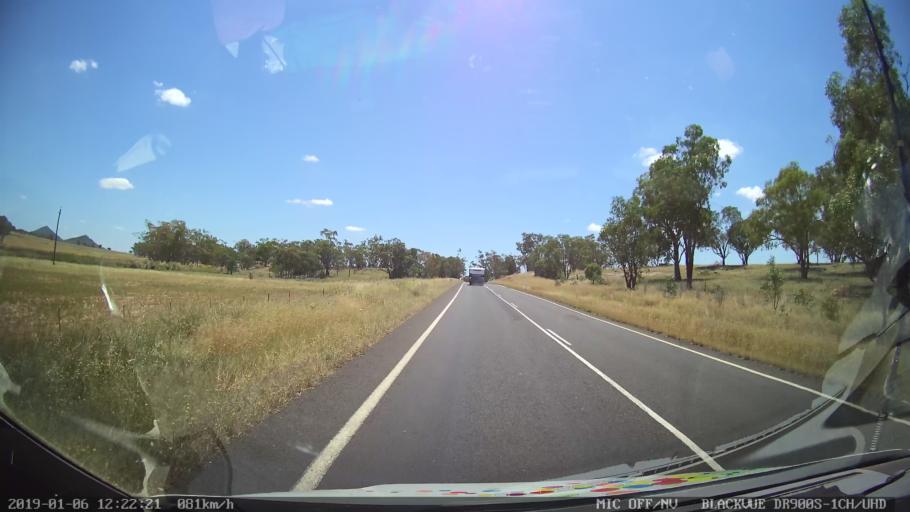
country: AU
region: New South Wales
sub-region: Tamworth Municipality
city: Phillip
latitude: -31.2628
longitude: 150.7873
